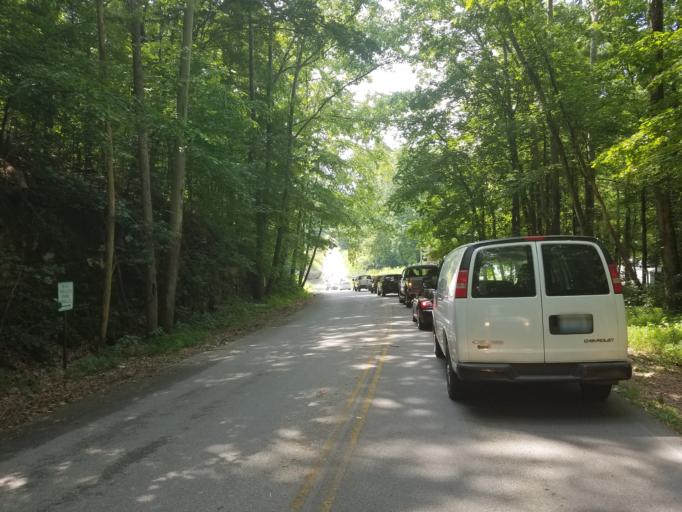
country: US
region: Kentucky
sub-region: Edmonson County
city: Brownsville
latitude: 37.1793
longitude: -86.1108
